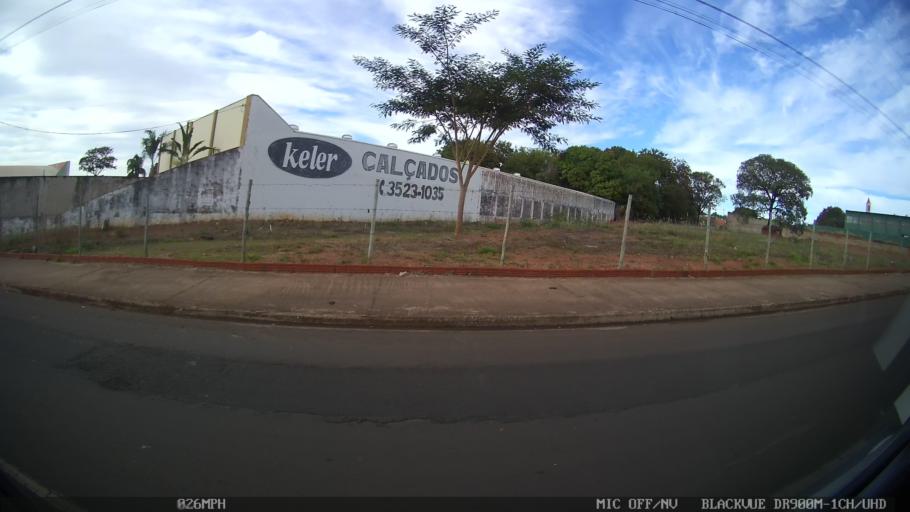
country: BR
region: Sao Paulo
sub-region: Catanduva
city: Catanduva
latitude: -21.1221
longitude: -48.9926
